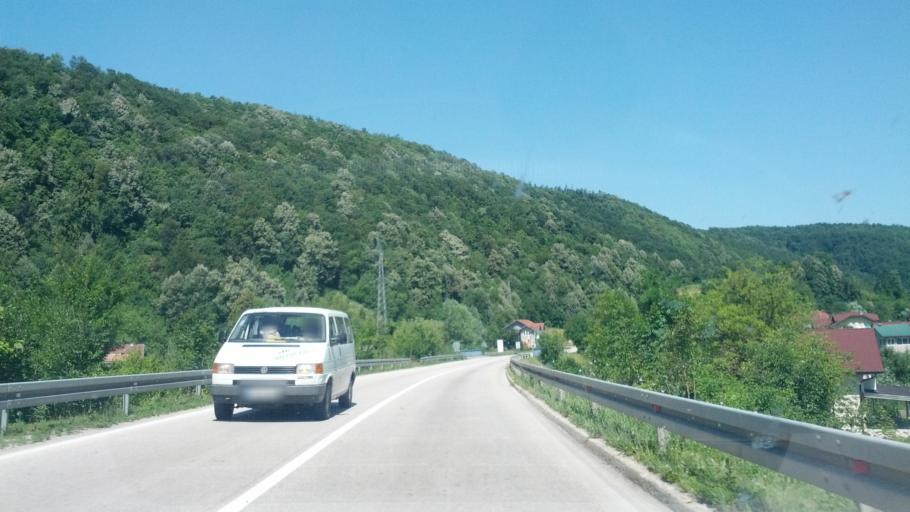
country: BA
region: Federation of Bosnia and Herzegovina
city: Bosanska Krupa
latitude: 44.9164
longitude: 16.1490
